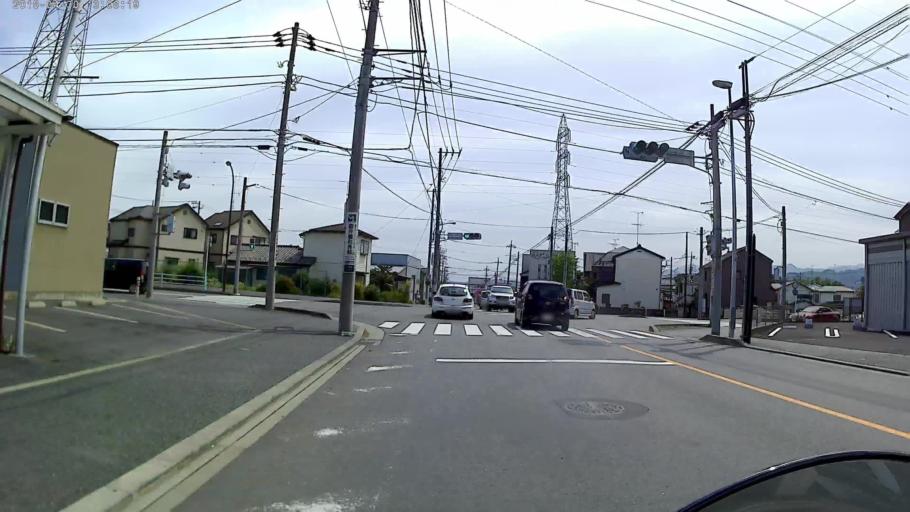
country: JP
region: Tokyo
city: Hachioji
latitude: 35.5914
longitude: 139.3214
